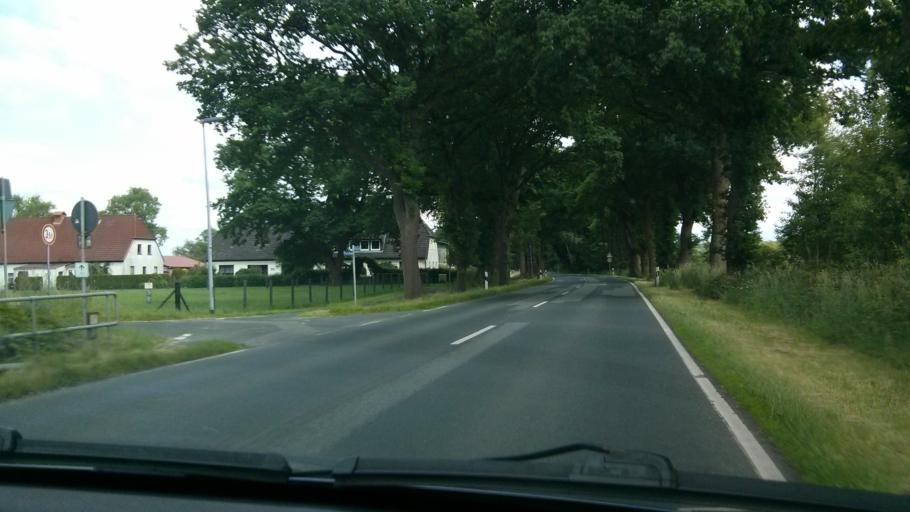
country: DE
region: Lower Saxony
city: Schiffdorf
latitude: 53.5152
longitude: 8.6908
